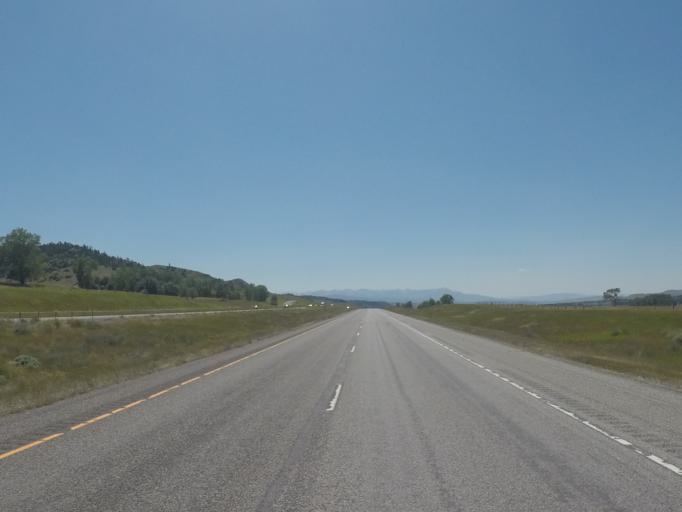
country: US
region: Montana
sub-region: Sweet Grass County
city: Big Timber
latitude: 45.8020
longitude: -110.0259
